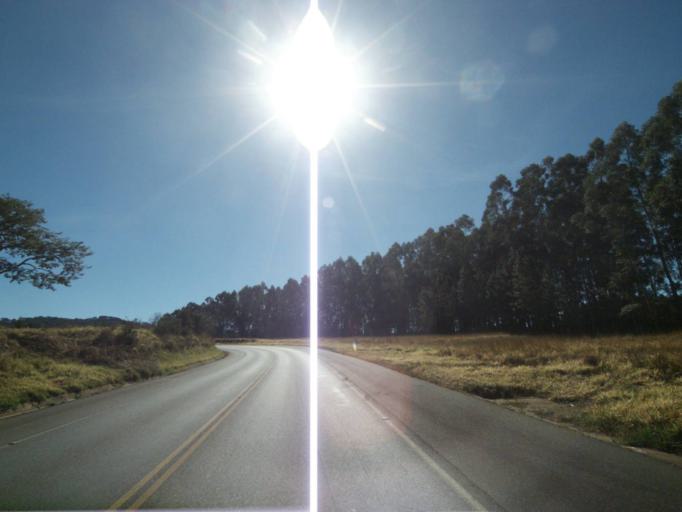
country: BR
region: Parana
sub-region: Tibagi
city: Tibagi
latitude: -24.5135
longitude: -50.4370
